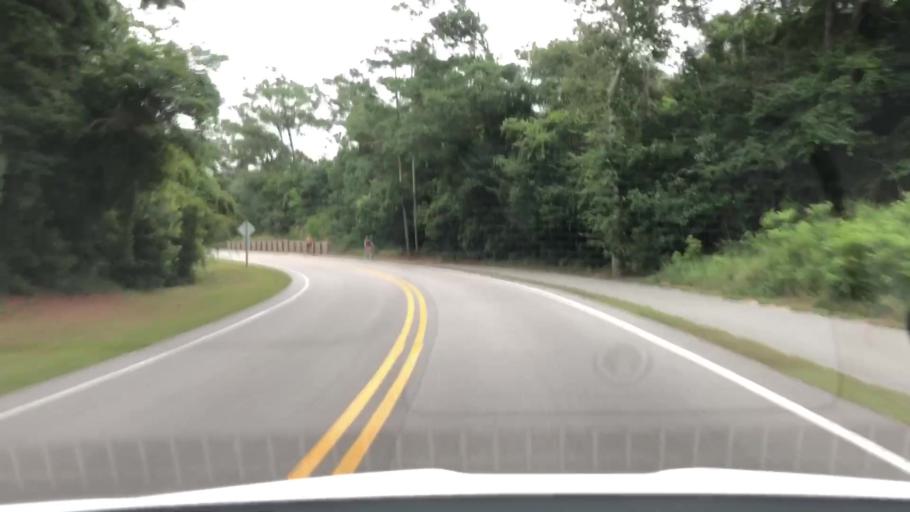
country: US
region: North Carolina
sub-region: Carteret County
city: Cedar Point
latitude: 34.6568
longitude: -77.0735
